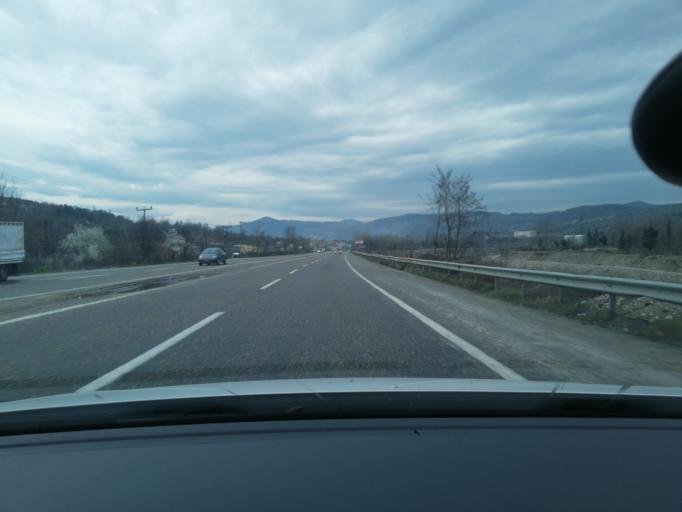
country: TR
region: Zonguldak
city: Devrek
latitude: 41.2497
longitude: 32.0110
